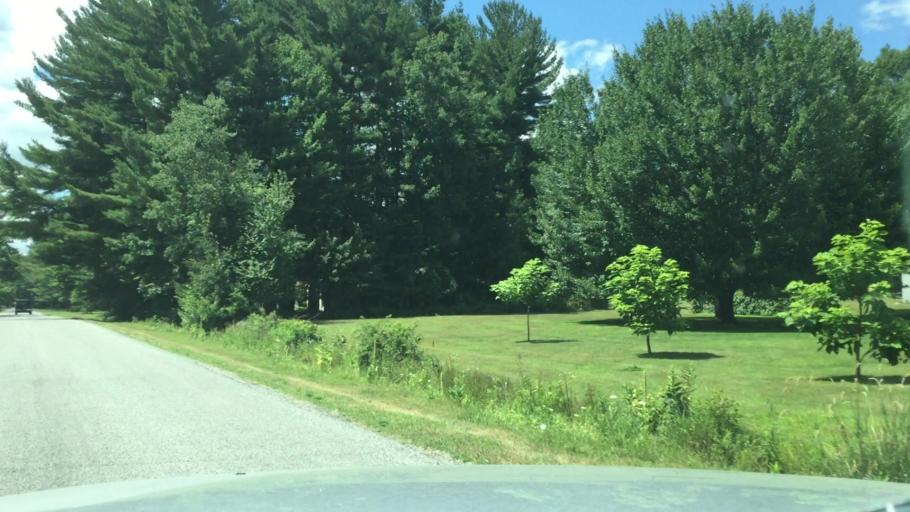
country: US
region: Michigan
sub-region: Saginaw County
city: Saint Charles
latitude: 43.3583
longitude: -84.1414
